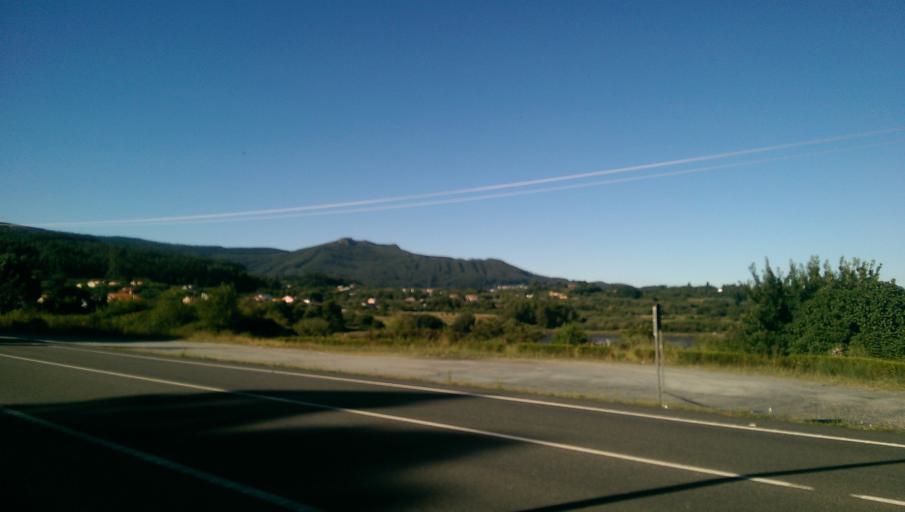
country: ES
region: Galicia
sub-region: Provincia da Coruna
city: Santa Marta de Ortigueira
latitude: 43.6686
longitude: -7.9024
